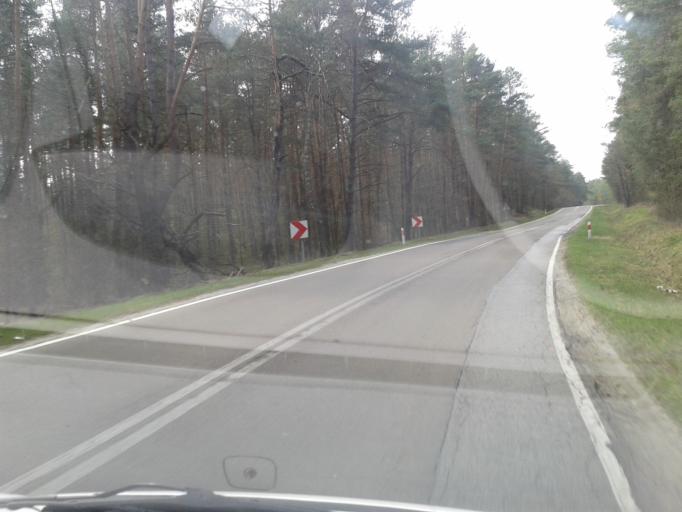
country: PL
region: Subcarpathian Voivodeship
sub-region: Powiat lubaczowski
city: Narol
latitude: 50.3713
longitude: 23.3683
